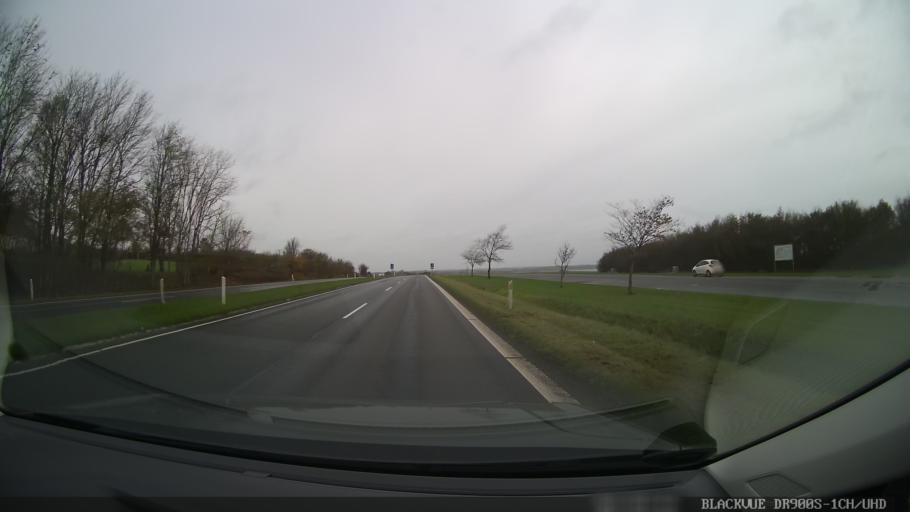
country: DK
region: North Denmark
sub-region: Thisted Kommune
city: Thisted
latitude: 56.8769
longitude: 8.6657
